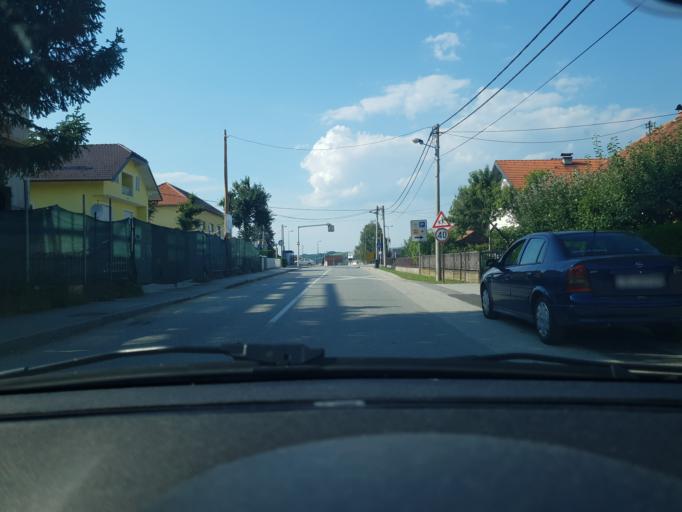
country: HR
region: Zagrebacka
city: Pojatno
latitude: 45.9313
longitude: 15.8150
